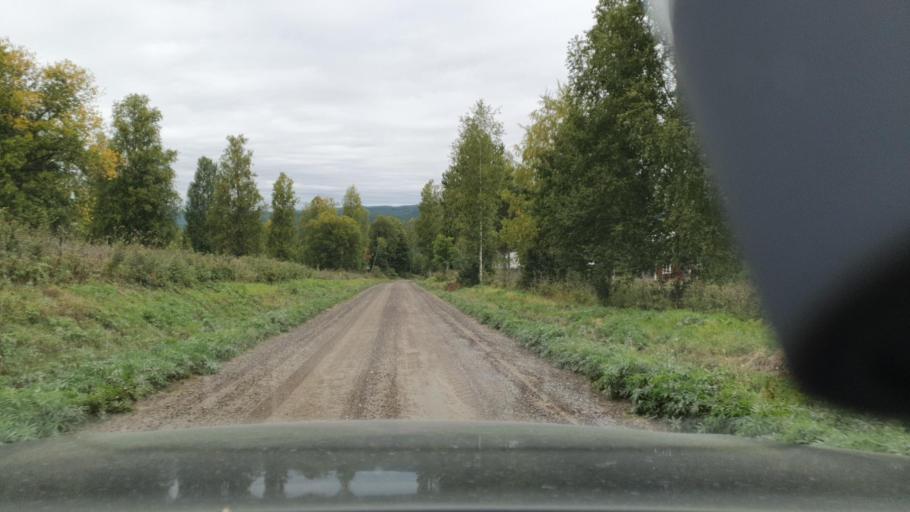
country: SE
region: Vaermland
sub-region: Torsby Kommun
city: Torsby
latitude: 60.1819
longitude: 12.6455
